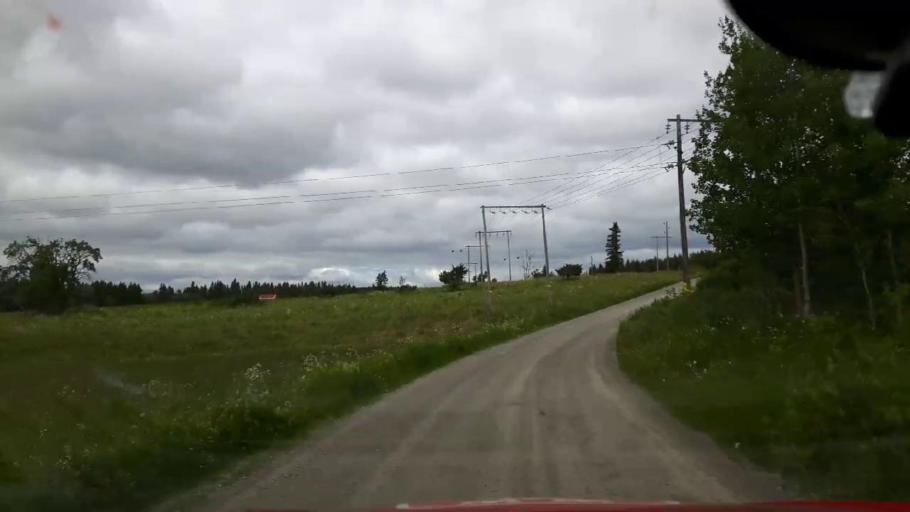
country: SE
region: Jaemtland
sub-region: OEstersunds Kommun
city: Brunflo
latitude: 63.0923
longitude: 14.8238
